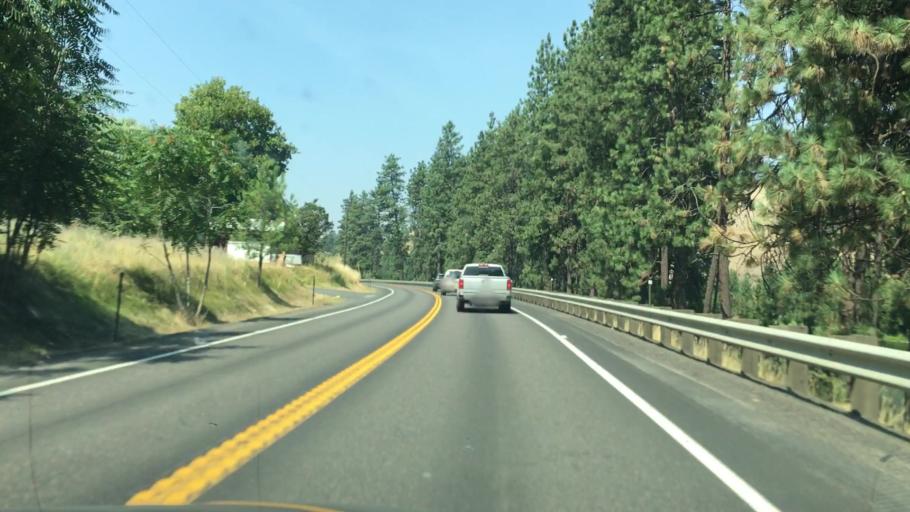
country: US
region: Idaho
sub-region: Clearwater County
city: Orofino
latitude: 46.4999
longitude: -116.4738
